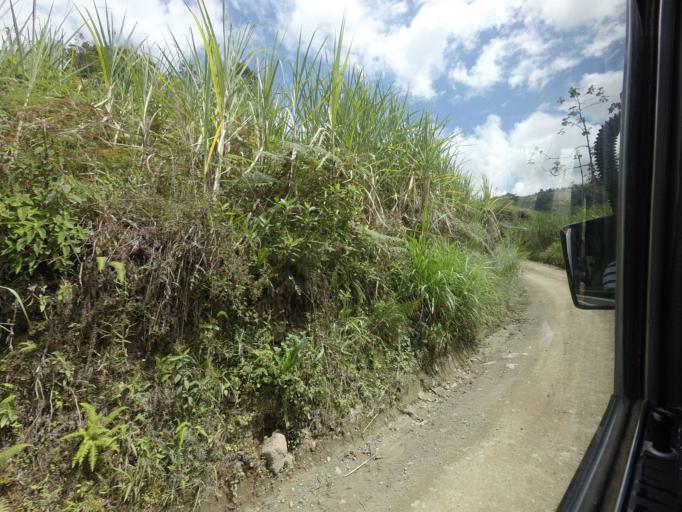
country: CO
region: Huila
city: Isnos
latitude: 1.9573
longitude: -76.2826
